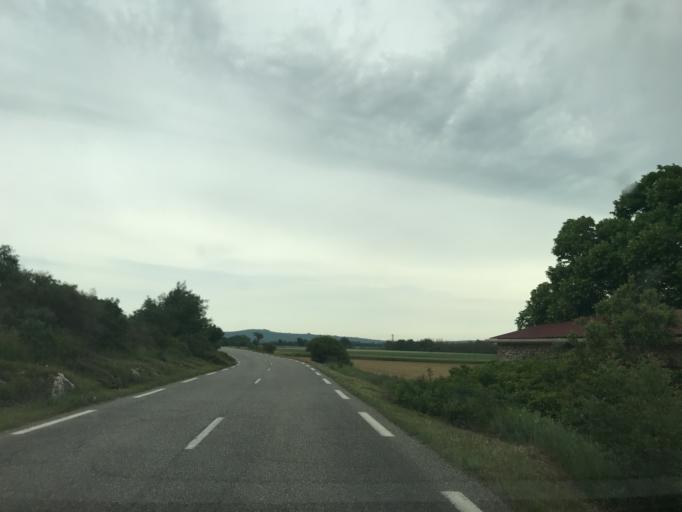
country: FR
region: Provence-Alpes-Cote d'Azur
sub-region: Departement du Var
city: Ginasservis
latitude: 43.6423
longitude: 5.8100
